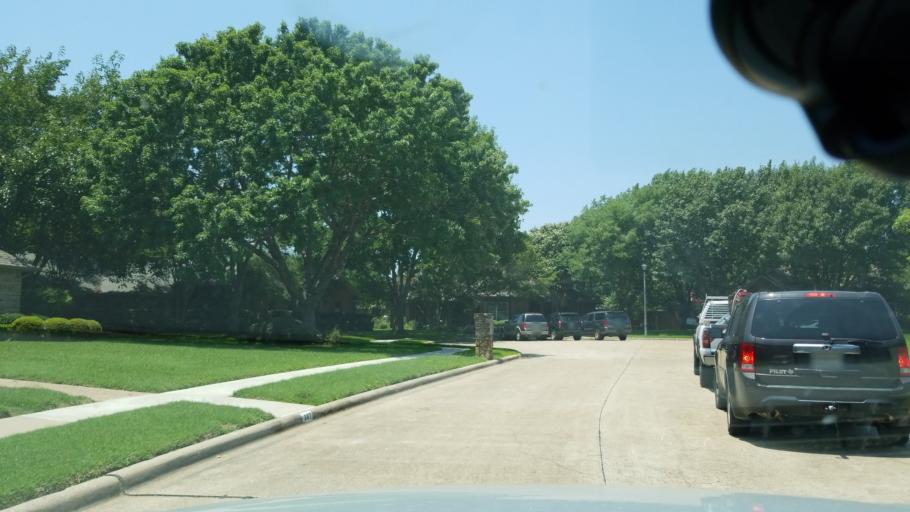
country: US
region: Texas
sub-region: Dallas County
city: Coppell
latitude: 32.9614
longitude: -96.9968
